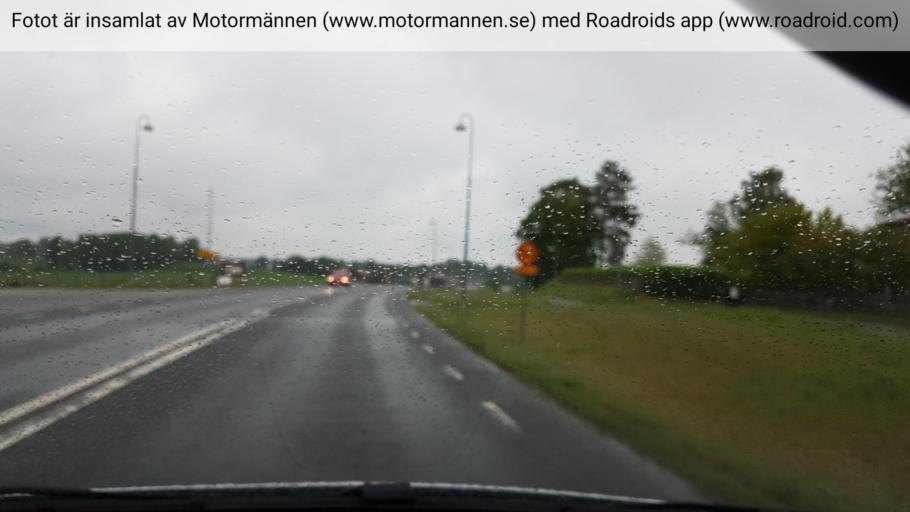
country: SE
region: Vaestra Goetaland
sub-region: Falkopings Kommun
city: Falkoeping
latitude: 57.9790
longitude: 13.5277
